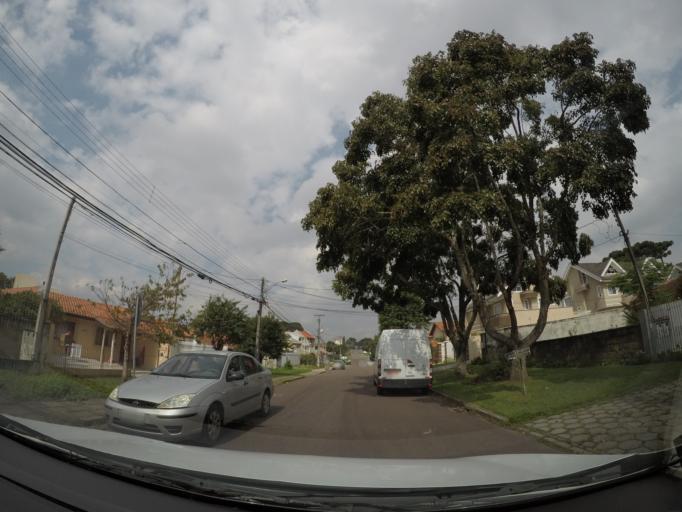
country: BR
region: Parana
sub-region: Sao Jose Dos Pinhais
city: Sao Jose dos Pinhais
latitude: -25.5016
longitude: -49.2486
